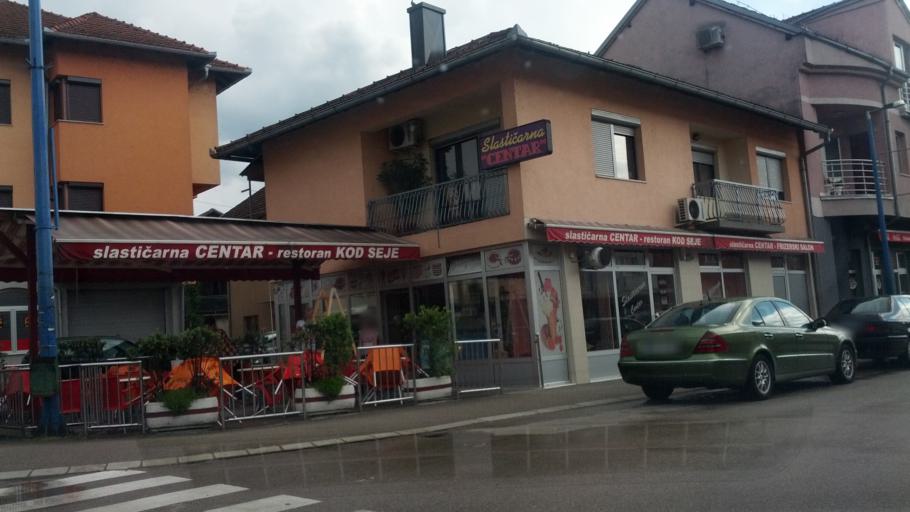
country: BA
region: Federation of Bosnia and Herzegovina
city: Bosanska Krupa
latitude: 44.8843
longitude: 16.1536
